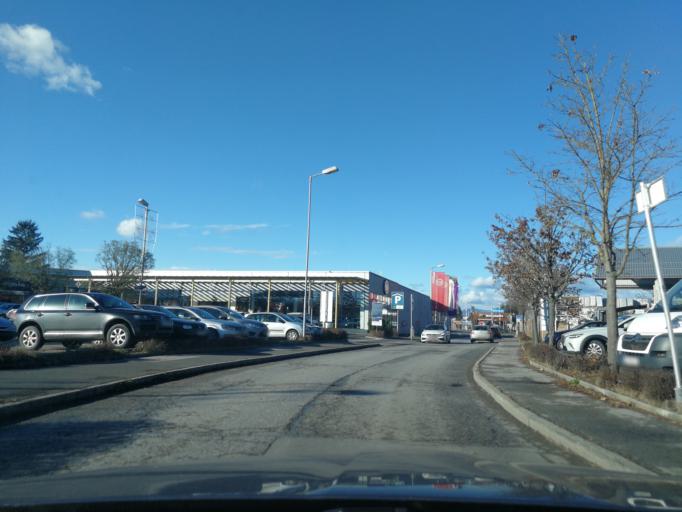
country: AT
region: Styria
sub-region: Politischer Bezirk Weiz
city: Gleisdorf
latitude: 47.1068
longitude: 15.7050
